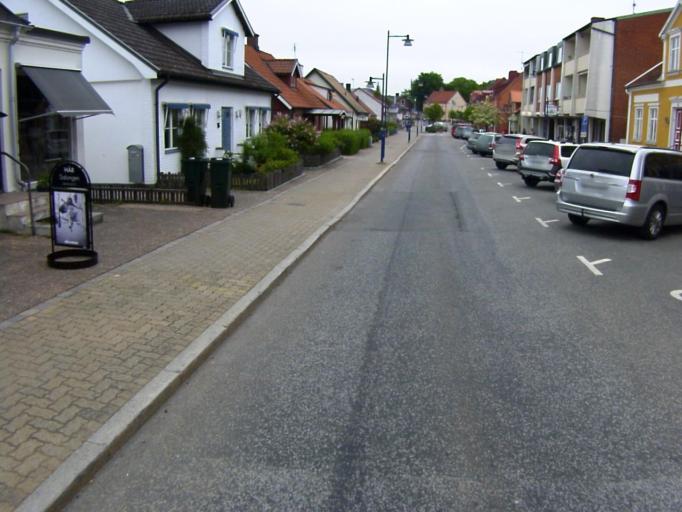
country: SE
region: Skane
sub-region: Kristianstads Kommun
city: Ahus
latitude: 55.9253
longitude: 14.2993
